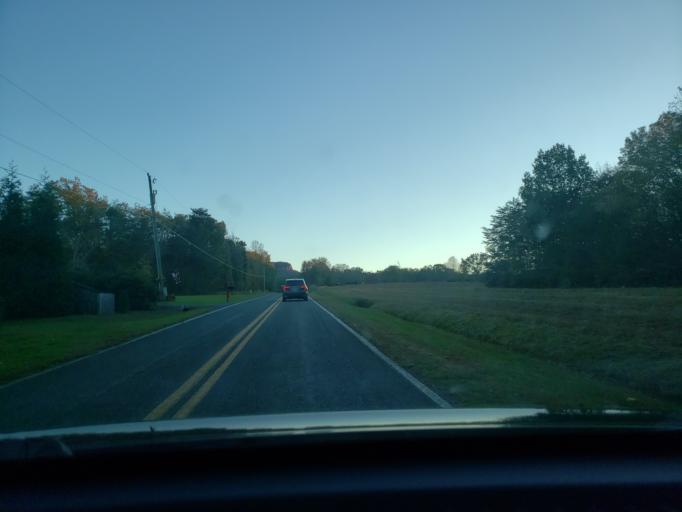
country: US
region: North Carolina
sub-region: Stokes County
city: Danbury
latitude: 36.4205
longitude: -80.2437
